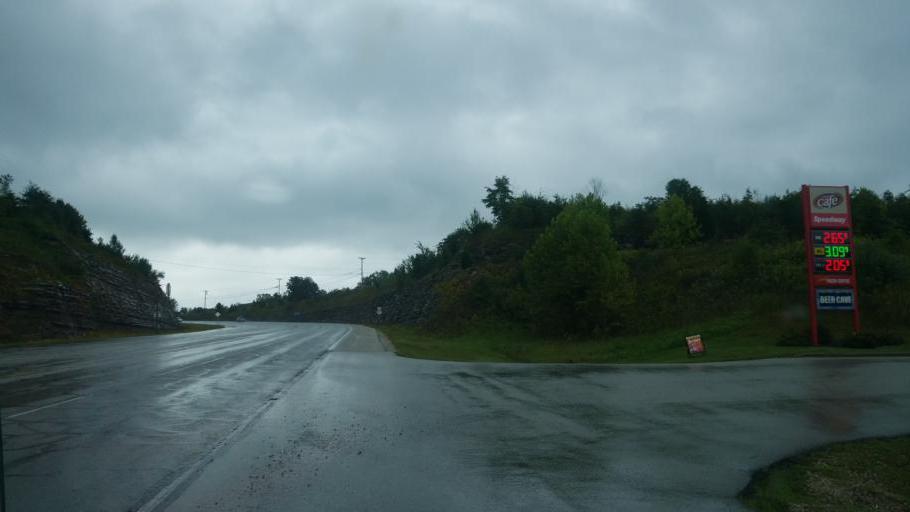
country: US
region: Kentucky
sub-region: Rowan County
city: Morehead
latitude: 38.2016
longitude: -83.4756
